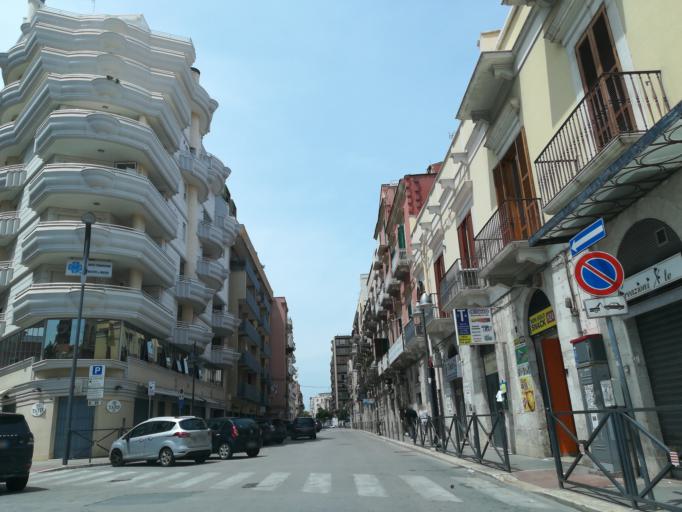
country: IT
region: Apulia
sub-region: Provincia di Barletta - Andria - Trani
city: Barletta
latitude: 41.3183
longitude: 16.2808
